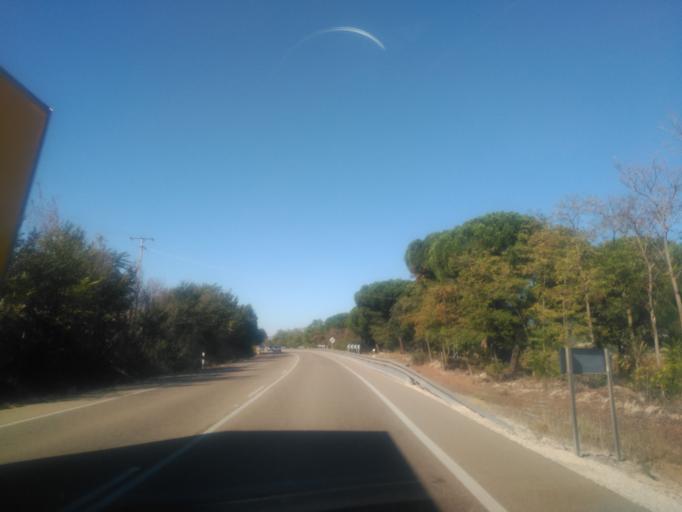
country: ES
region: Castille and Leon
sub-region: Provincia de Valladolid
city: Valbuena de Duero
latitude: 41.6282
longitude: -4.2867
